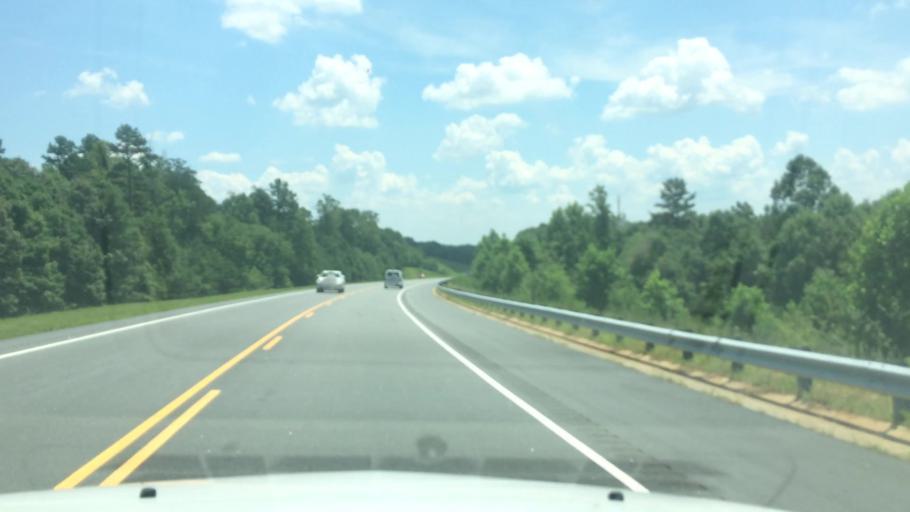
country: US
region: North Carolina
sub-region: Alexander County
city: Stony Point
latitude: 35.8851
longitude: -81.0768
